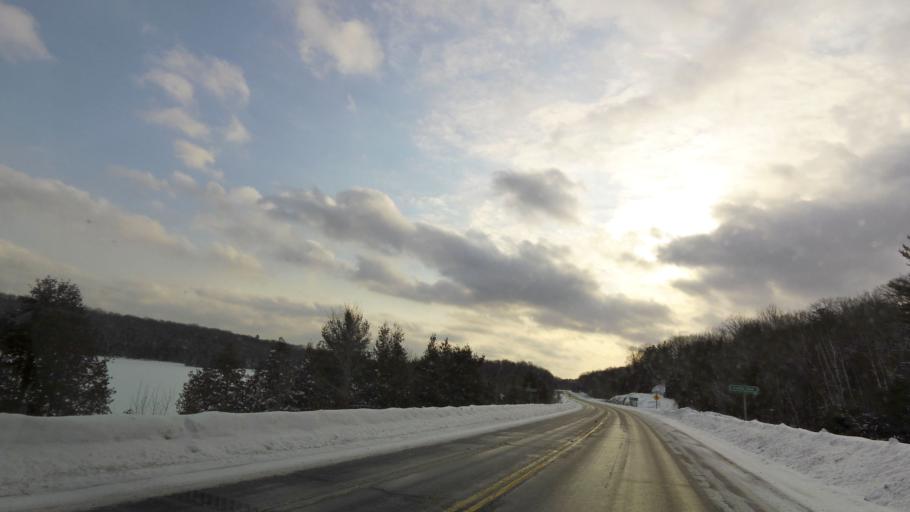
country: CA
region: Ontario
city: Bracebridge
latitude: 44.8139
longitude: -78.7951
